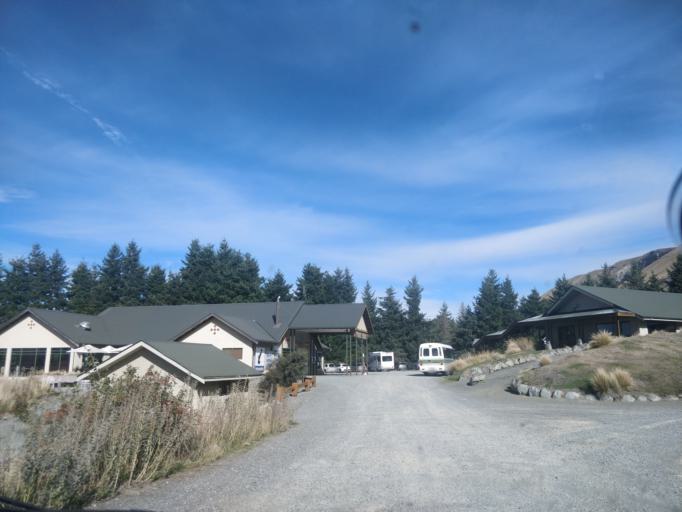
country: NZ
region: Canterbury
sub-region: Timaru District
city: Pleasant Point
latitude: -43.9114
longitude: 170.1211
